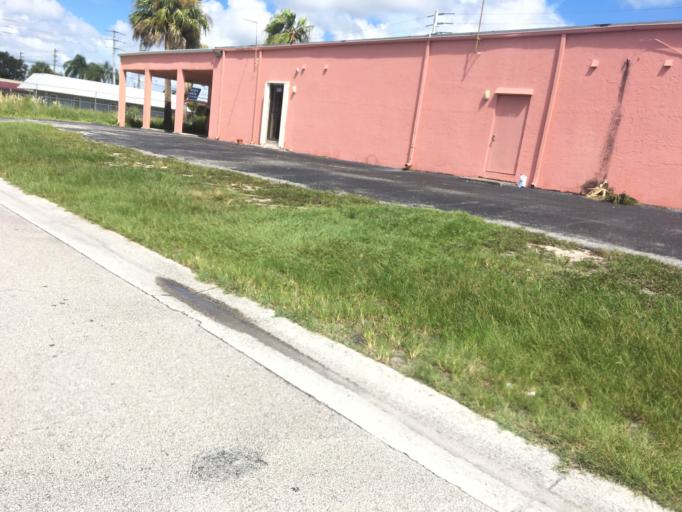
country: US
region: Florida
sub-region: Martin County
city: Palm City
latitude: 27.1718
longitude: -80.2669
